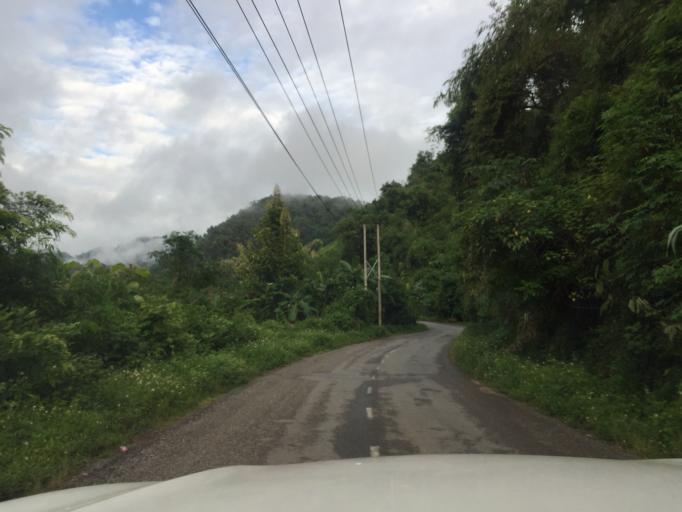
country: LA
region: Phongsali
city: Khoa
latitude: 21.1030
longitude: 102.2688
